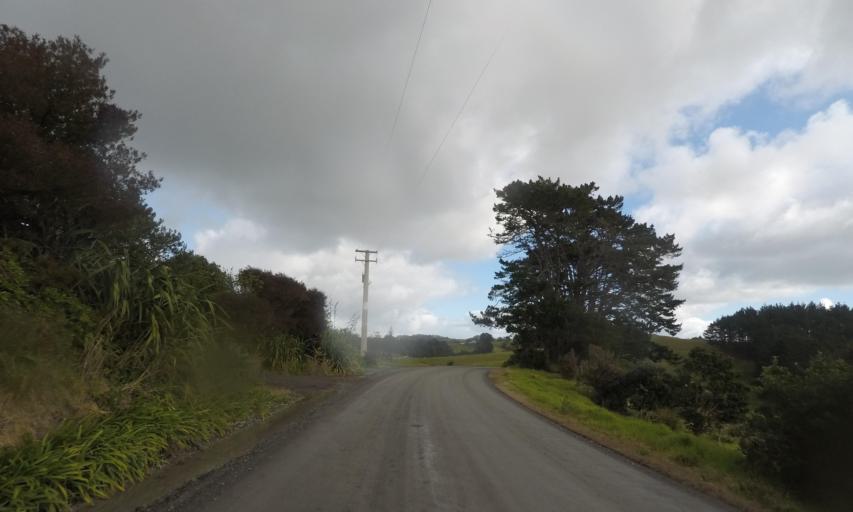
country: NZ
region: Auckland
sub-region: Auckland
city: Wellsford
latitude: -36.1736
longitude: 174.5973
